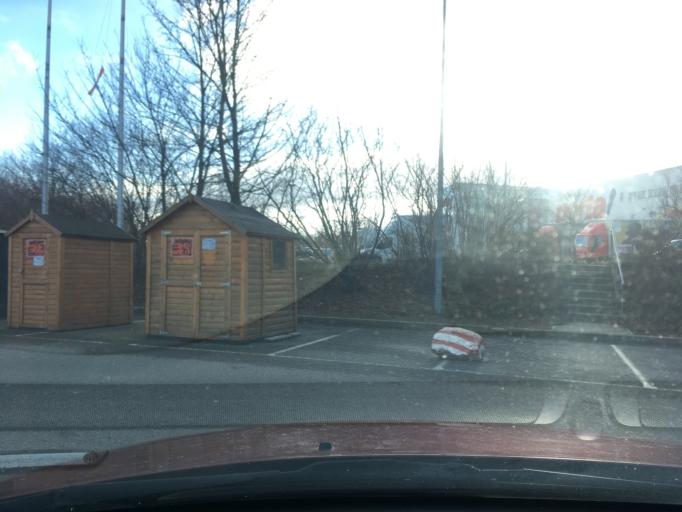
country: DE
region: Saxony
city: Goerlitz
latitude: 51.1902
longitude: 14.9577
